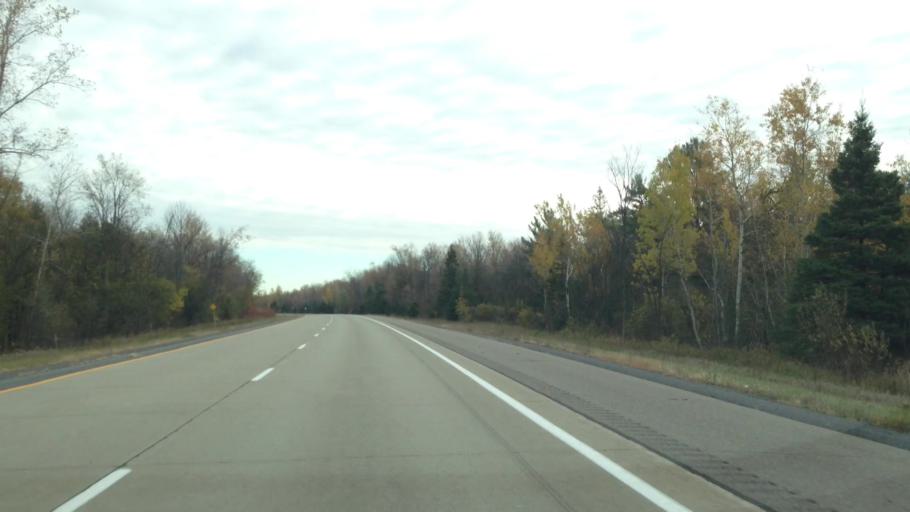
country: CA
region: Ontario
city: Casselman
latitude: 45.3807
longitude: -74.8093
